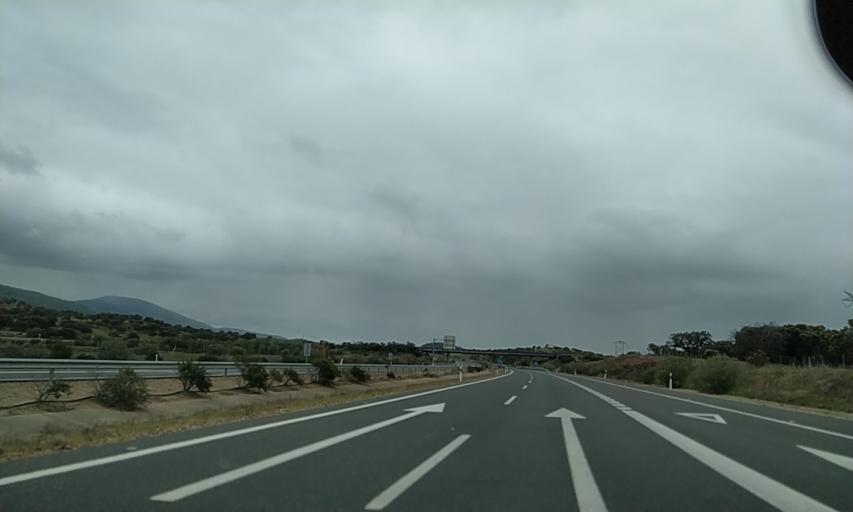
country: ES
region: Extremadura
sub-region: Provincia de Caceres
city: Jarilla
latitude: 40.1876
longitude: -6.0099
